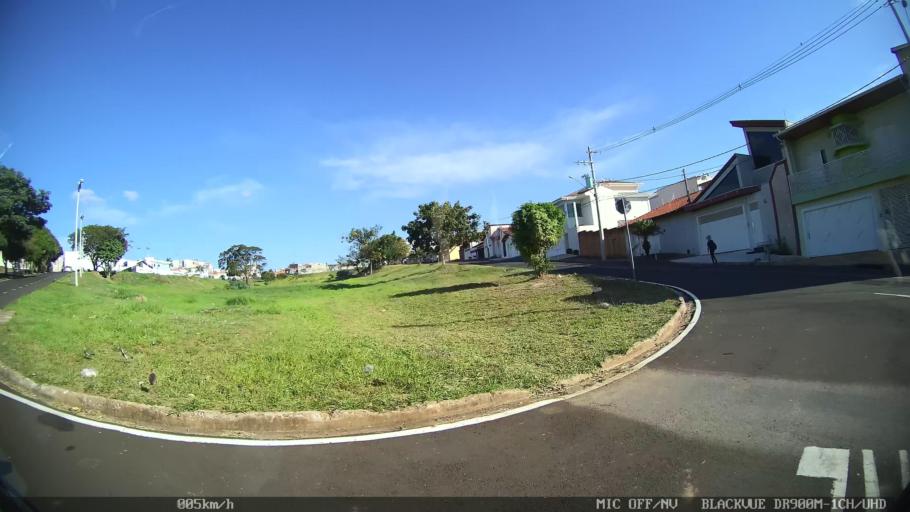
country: BR
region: Sao Paulo
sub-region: Franca
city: Franca
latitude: -20.5235
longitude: -47.4159
